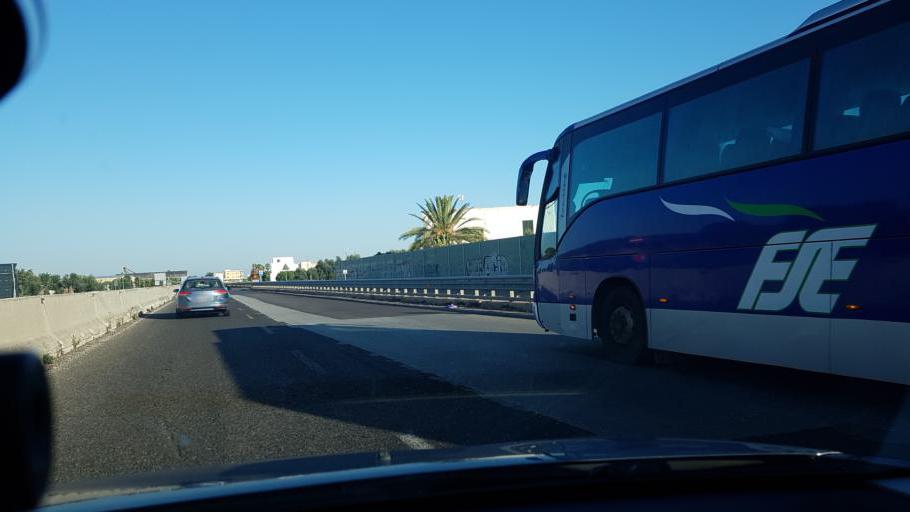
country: IT
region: Apulia
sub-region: Provincia di Brindisi
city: Fasano
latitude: 40.8541
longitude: 17.3541
